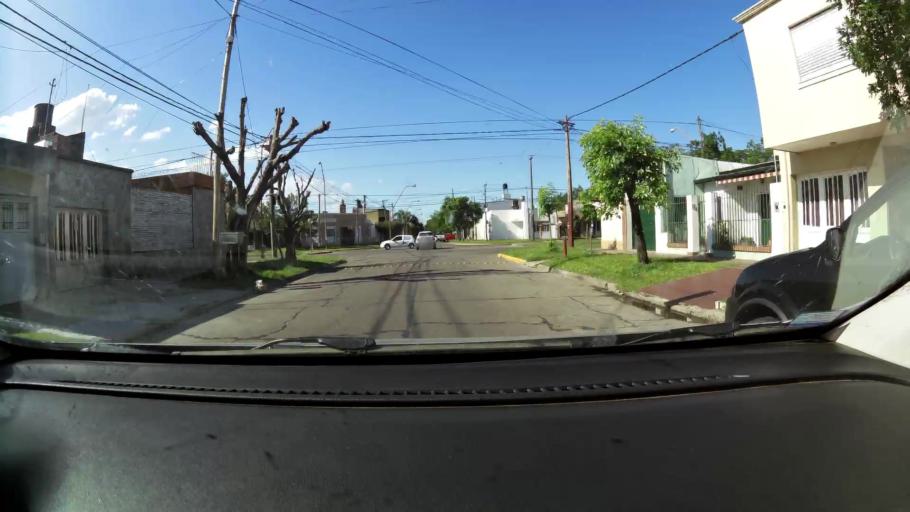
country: AR
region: Santa Fe
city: Santa Fe de la Vera Cruz
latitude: -31.6076
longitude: -60.6834
